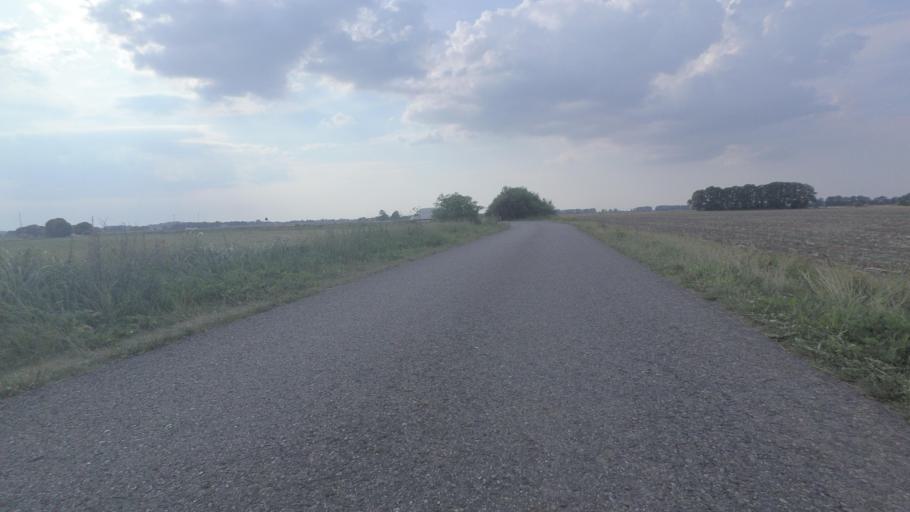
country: DE
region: Brandenburg
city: Wittstock
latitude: 53.2417
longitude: 12.4579
